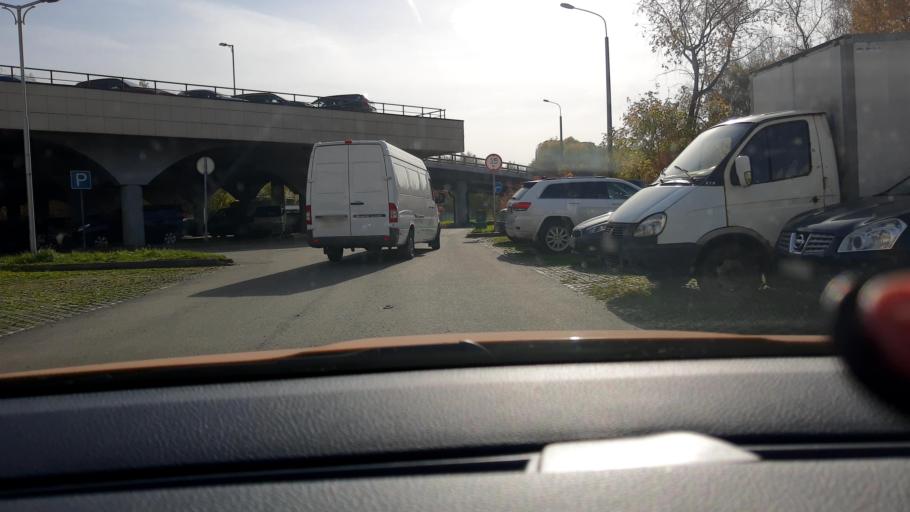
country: RU
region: Moscow
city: Babushkin
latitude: 55.8778
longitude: 37.7288
